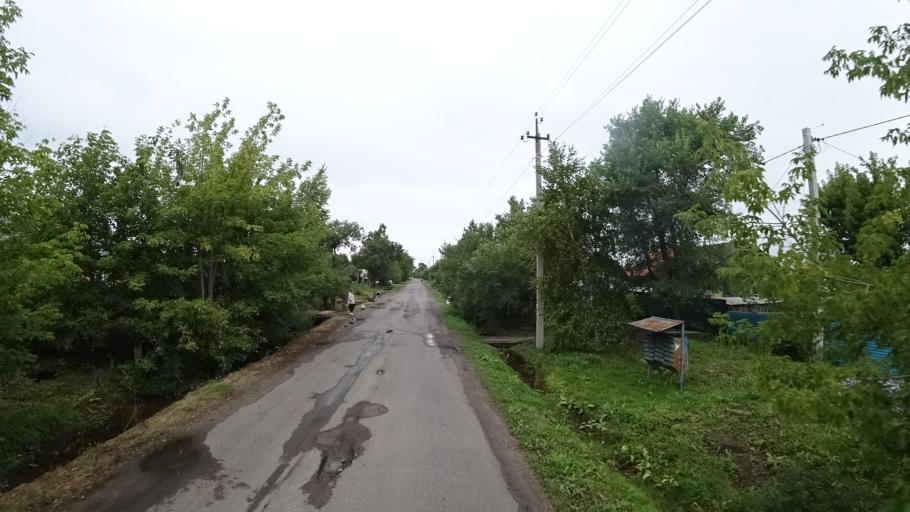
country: RU
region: Primorskiy
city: Chernigovka
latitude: 44.3412
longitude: 132.5875
